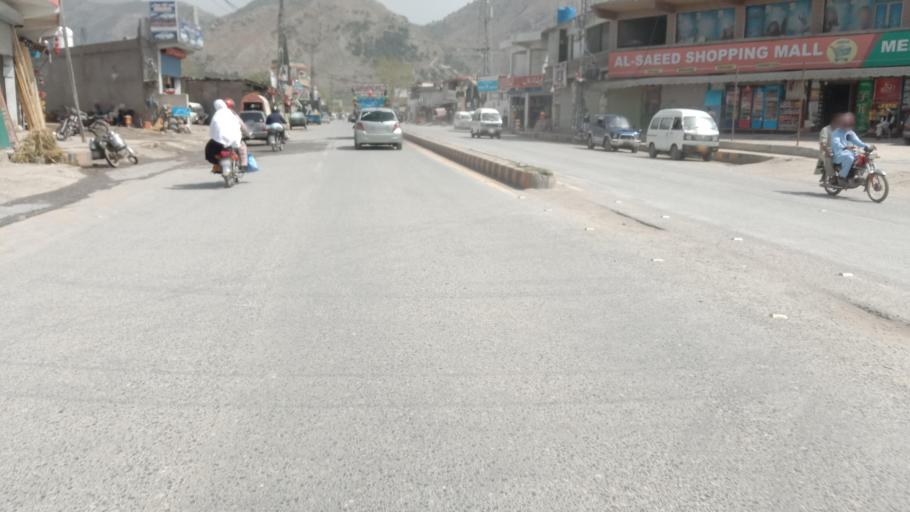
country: PK
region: Khyber Pakhtunkhwa
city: Abbottabad
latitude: 34.1579
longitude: 73.2582
